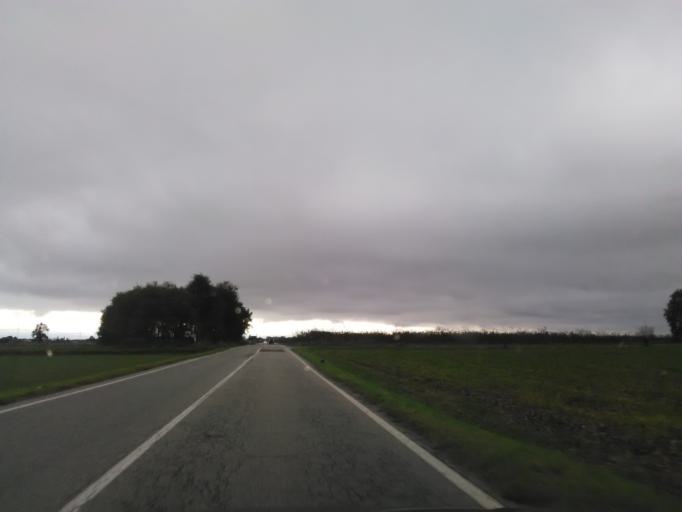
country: IT
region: Piedmont
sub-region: Provincia di Vercelli
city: Borgo d'Ale
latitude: 45.3305
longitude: 8.0390
